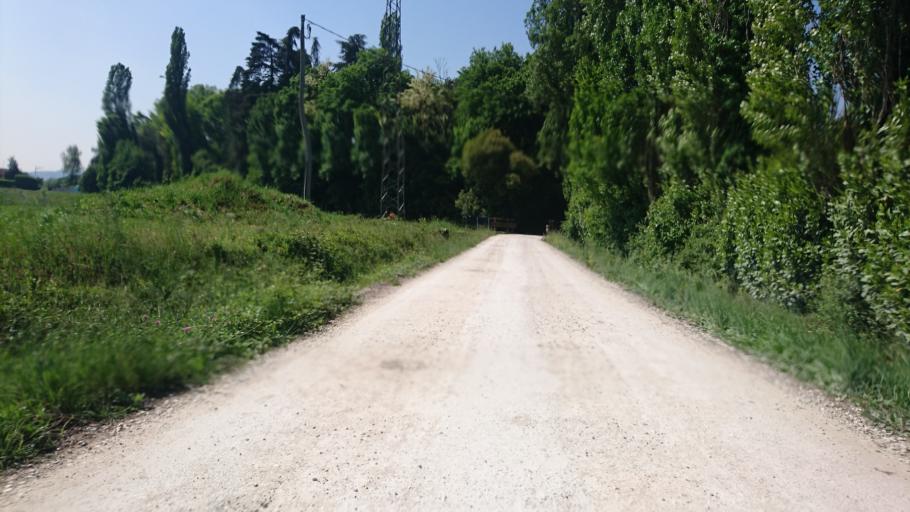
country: IT
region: Veneto
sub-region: Provincia di Padova
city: San Biagio
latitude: 45.3688
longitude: 11.7624
